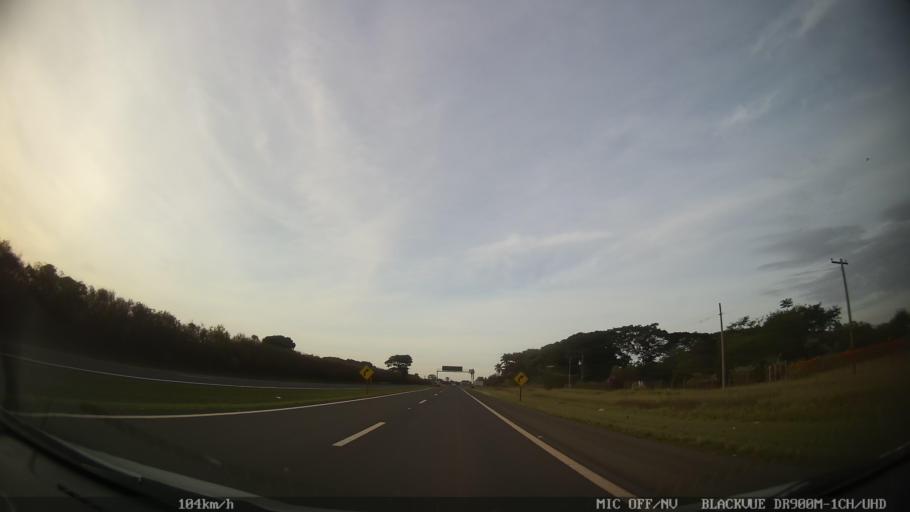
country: BR
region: Sao Paulo
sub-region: Iracemapolis
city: Iracemapolis
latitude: -22.6017
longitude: -47.4728
